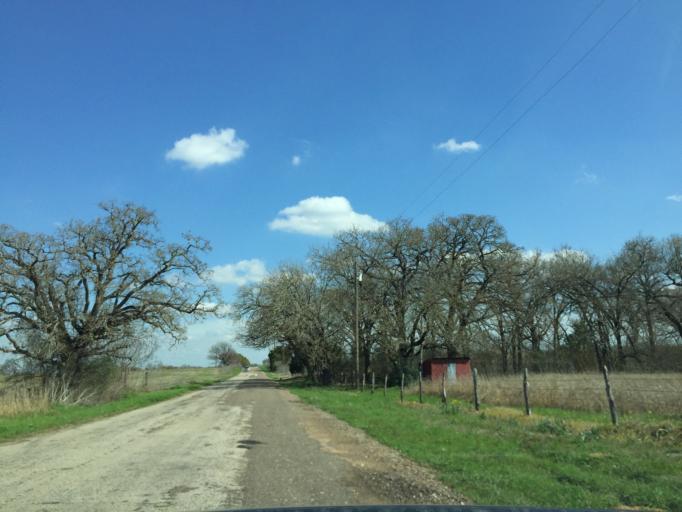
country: US
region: Texas
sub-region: Milam County
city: Thorndale
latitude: 30.5558
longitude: -97.1627
